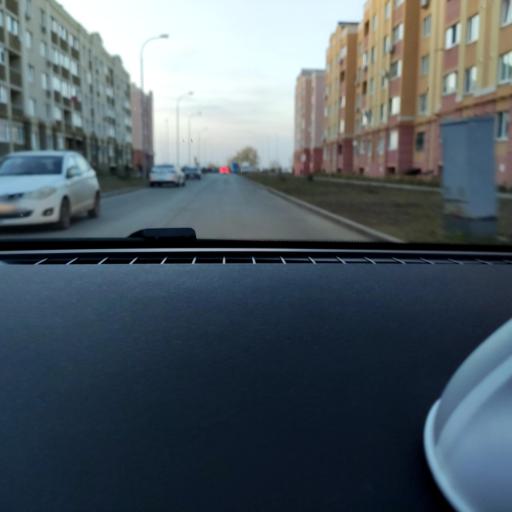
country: RU
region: Samara
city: Samara
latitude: 53.1176
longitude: 50.1574
